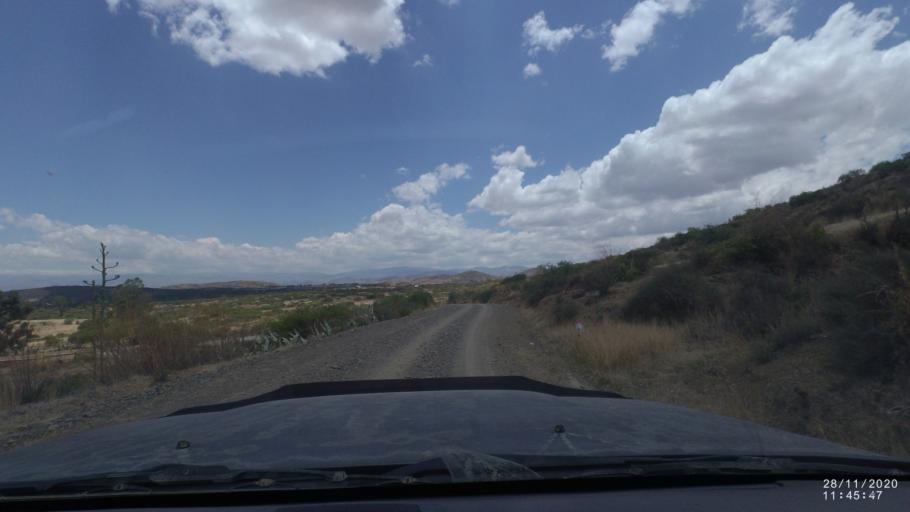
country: BO
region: Cochabamba
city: Tarata
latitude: -17.6537
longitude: -66.0438
